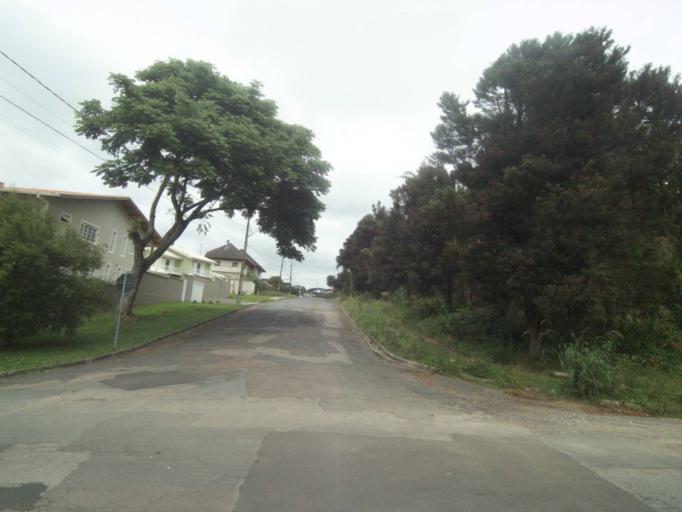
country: BR
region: Parana
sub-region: Curitiba
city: Curitiba
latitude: -25.3902
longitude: -49.2755
